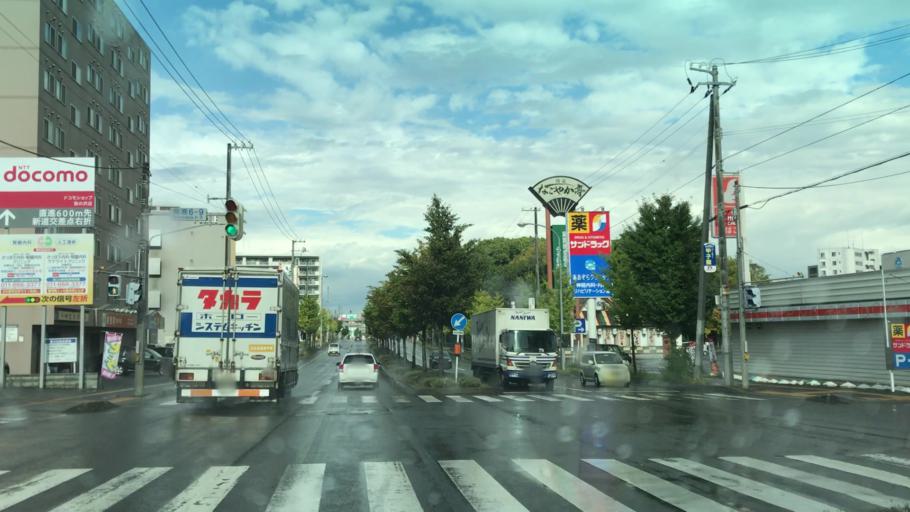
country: JP
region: Hokkaido
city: Sapporo
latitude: 43.0877
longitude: 141.2805
